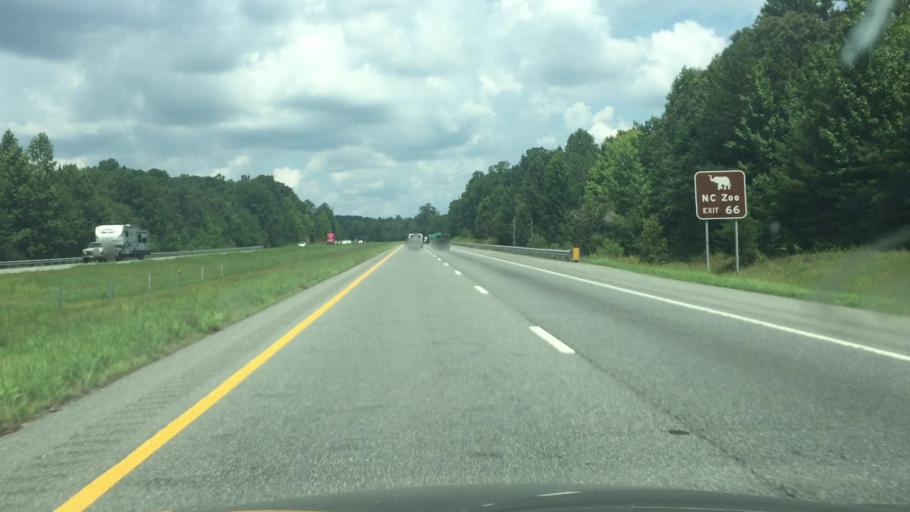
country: US
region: North Carolina
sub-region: Randolph County
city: Asheboro
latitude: 35.5784
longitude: -79.8063
